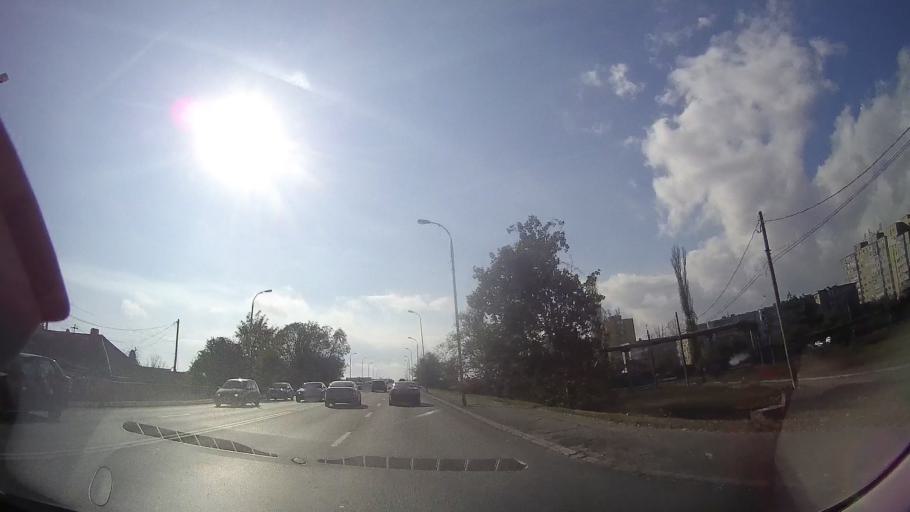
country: RO
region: Constanta
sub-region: Municipiul Constanta
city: Constanta
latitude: 44.1505
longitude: 28.6269
